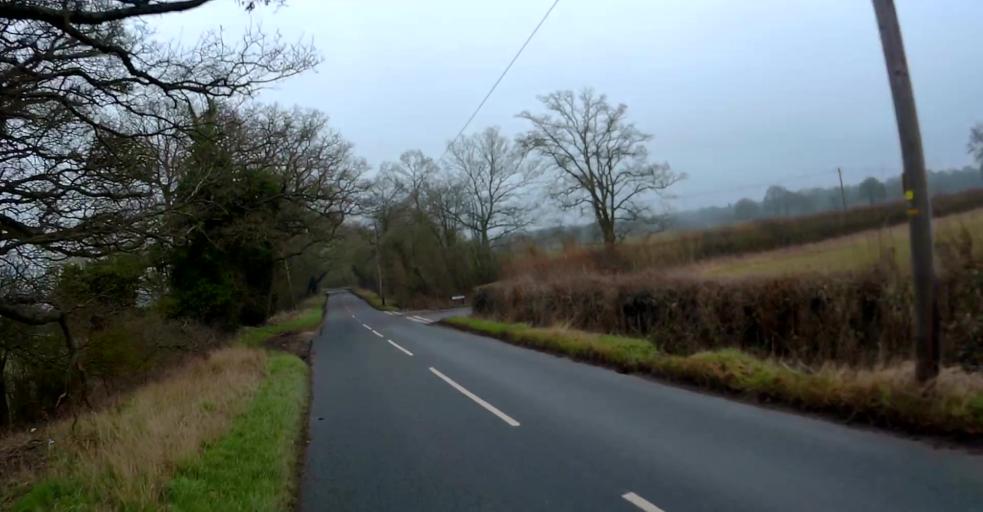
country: GB
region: England
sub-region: Hampshire
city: Old Basing
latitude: 51.2807
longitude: -1.0178
